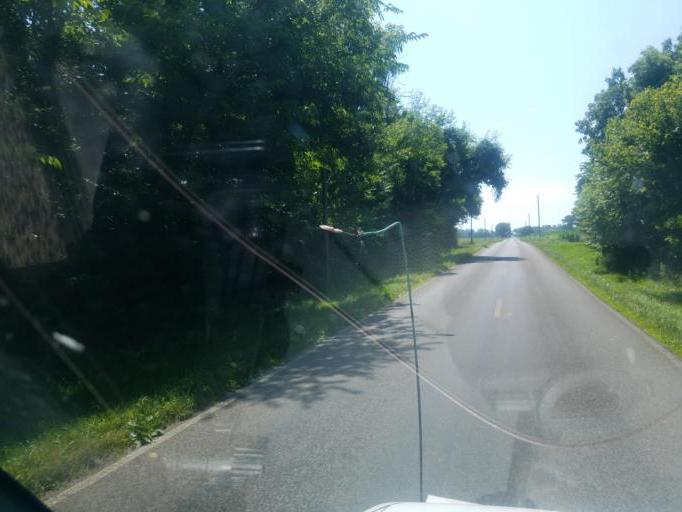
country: US
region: Ohio
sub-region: Champaign County
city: North Lewisburg
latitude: 40.2167
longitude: -83.5099
